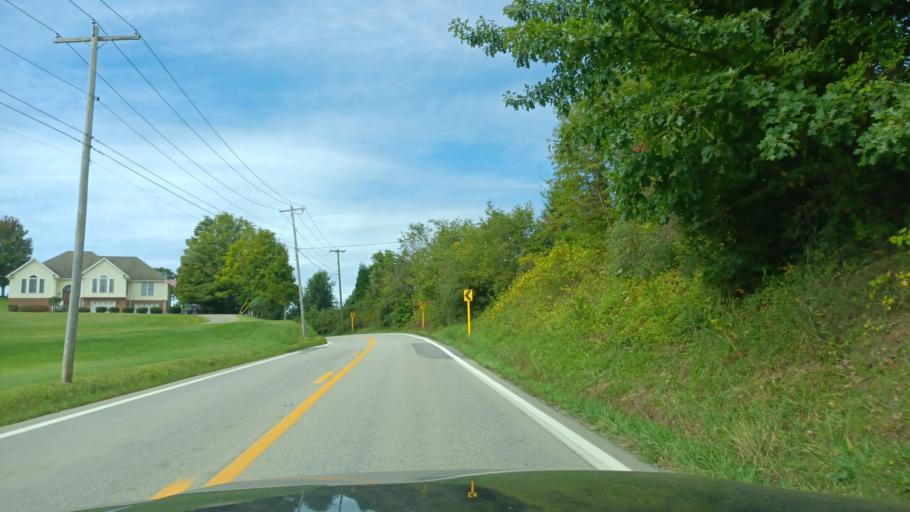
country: US
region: West Virginia
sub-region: Harrison County
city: Bridgeport
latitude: 39.3016
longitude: -80.1805
